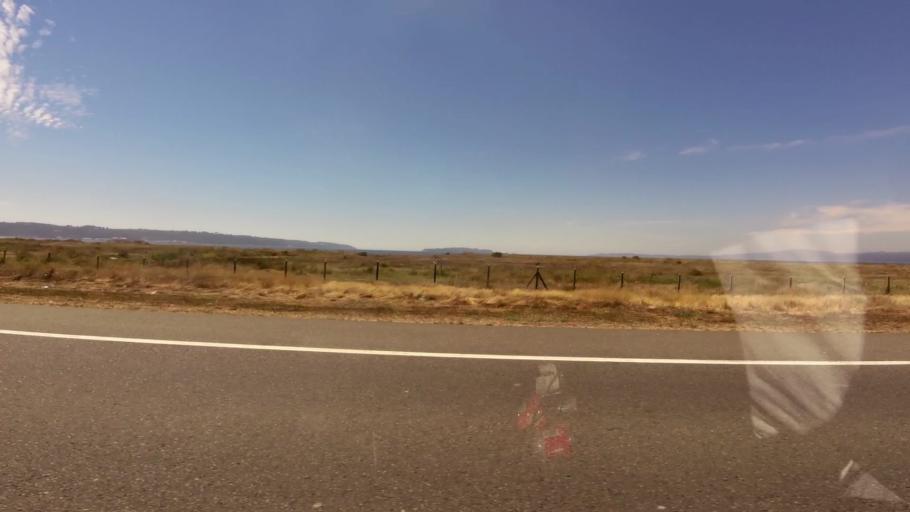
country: CL
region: Biobio
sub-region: Provincia de Concepcion
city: Talcahuano
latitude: -36.7335
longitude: -73.0704
